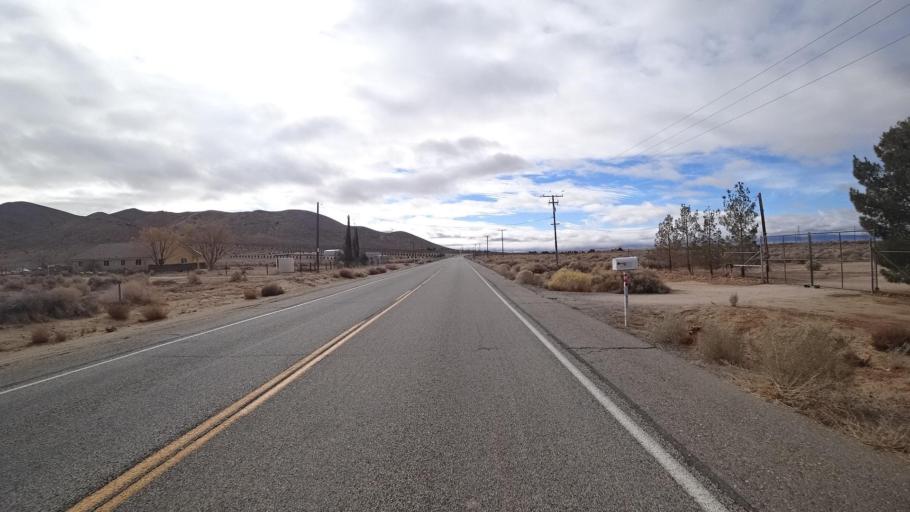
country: US
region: California
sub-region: Kern County
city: Rosamond
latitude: 34.8910
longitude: -118.2911
